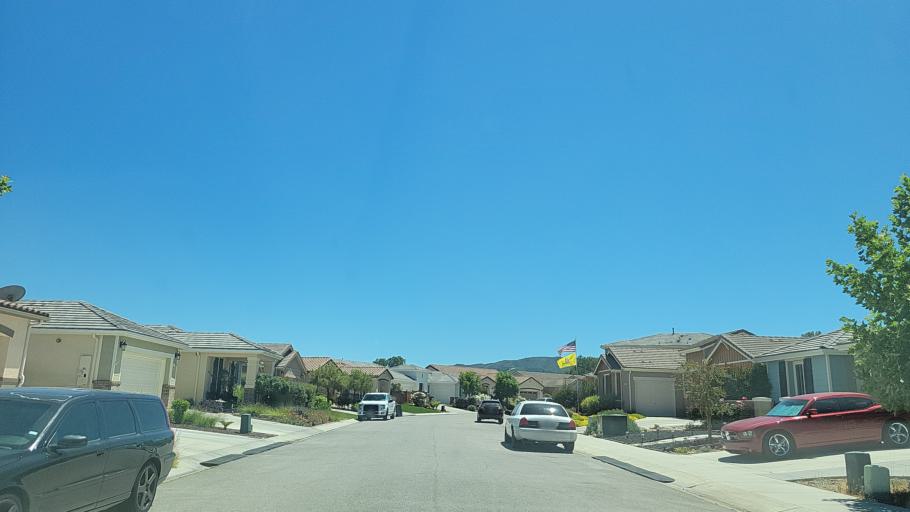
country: US
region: California
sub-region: San Luis Obispo County
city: Atascadero
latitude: 35.4515
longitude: -120.6268
